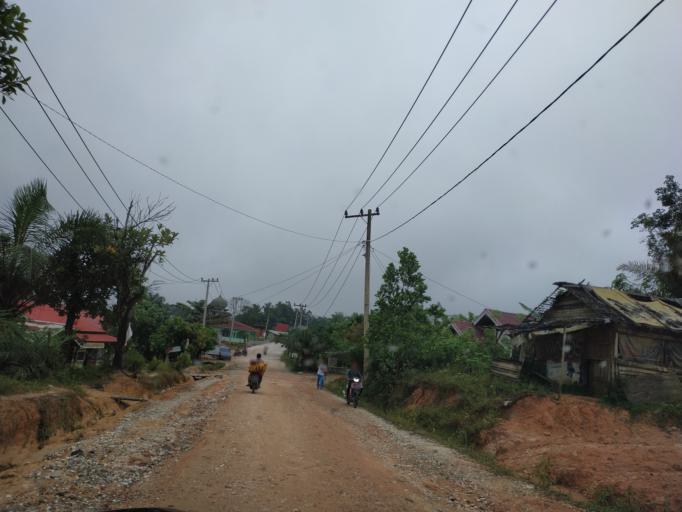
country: ID
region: Riau
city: Pekanbaru
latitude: 0.5045
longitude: 101.5289
